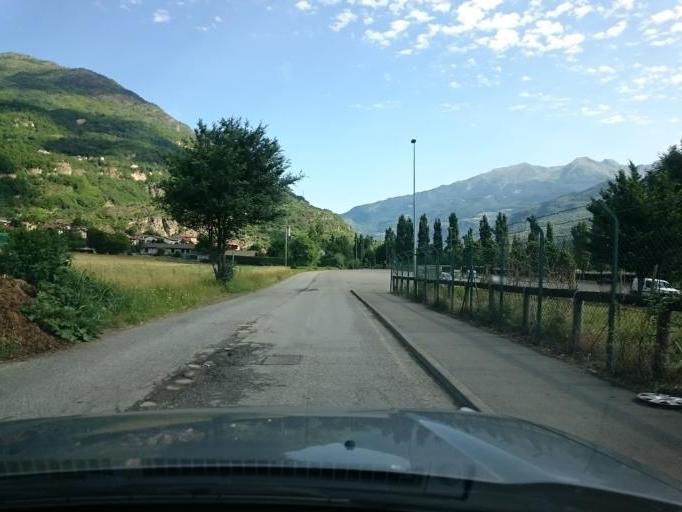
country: IT
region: Lombardy
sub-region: Provincia di Brescia
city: Capo di Ponte
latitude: 46.0235
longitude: 10.3422
